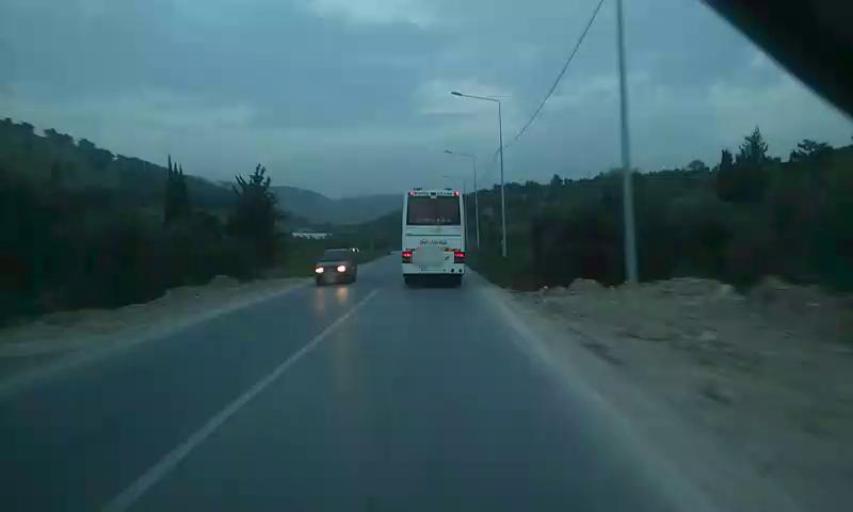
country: PS
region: West Bank
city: Kafr al Labad
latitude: 32.3170
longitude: 35.0886
